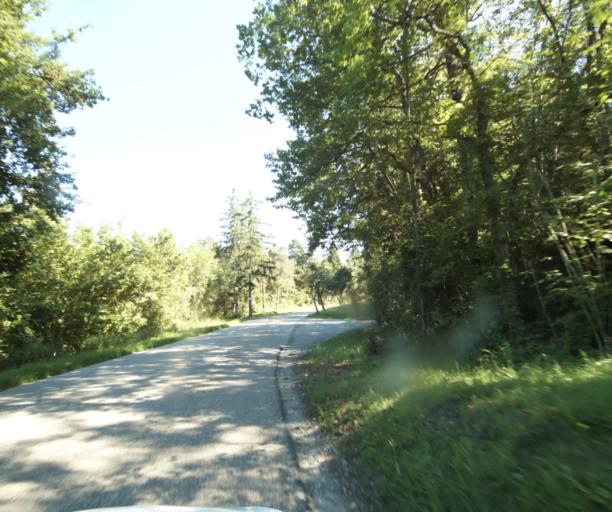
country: FR
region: Rhone-Alpes
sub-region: Departement de la Haute-Savoie
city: Sciez
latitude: 46.3179
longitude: 6.3856
